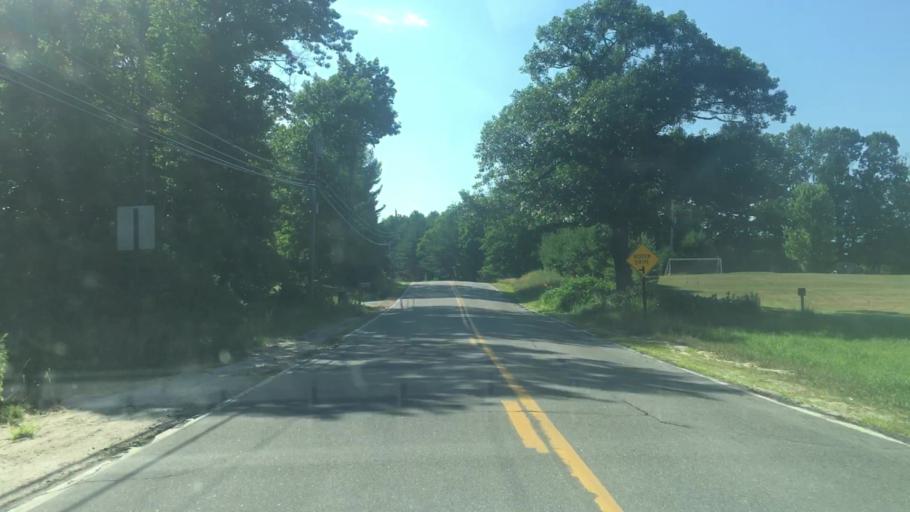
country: US
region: Maine
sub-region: York County
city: Hollis Center
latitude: 43.6330
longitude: -70.5671
